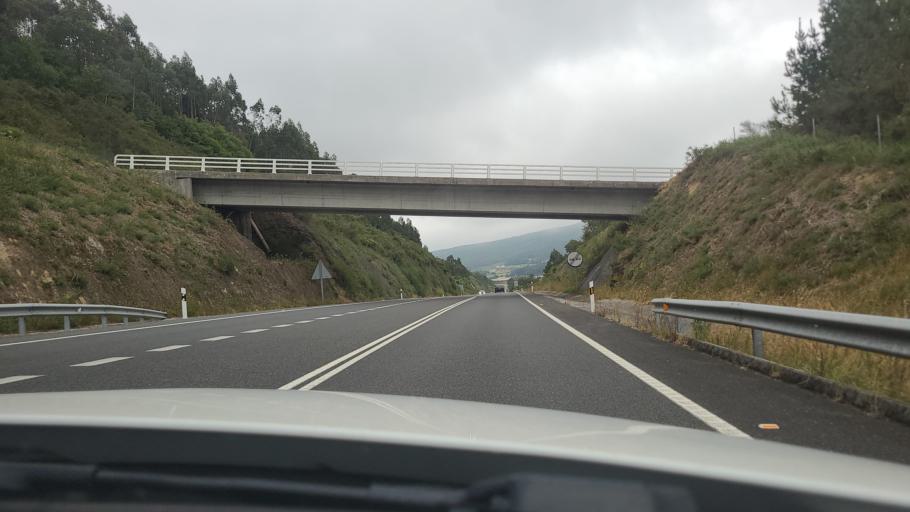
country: ES
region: Galicia
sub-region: Provincia da Coruna
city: Cee
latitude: 42.9655
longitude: -9.2070
